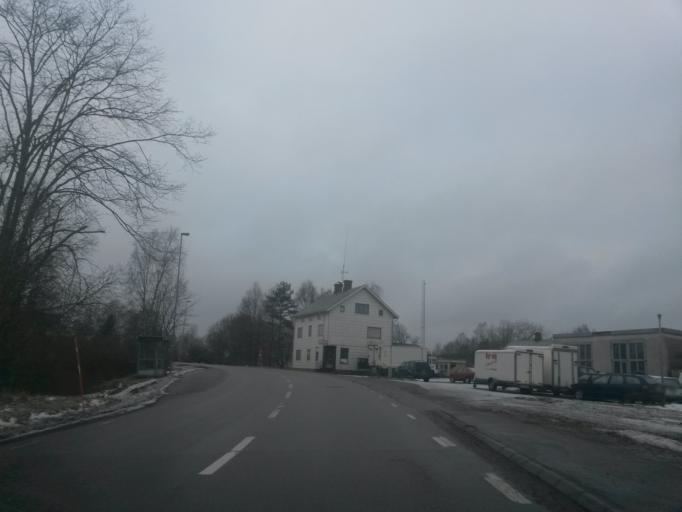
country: SE
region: Vaestra Goetaland
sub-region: Alingsas Kommun
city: Sollebrunn
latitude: 58.1138
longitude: 12.6321
